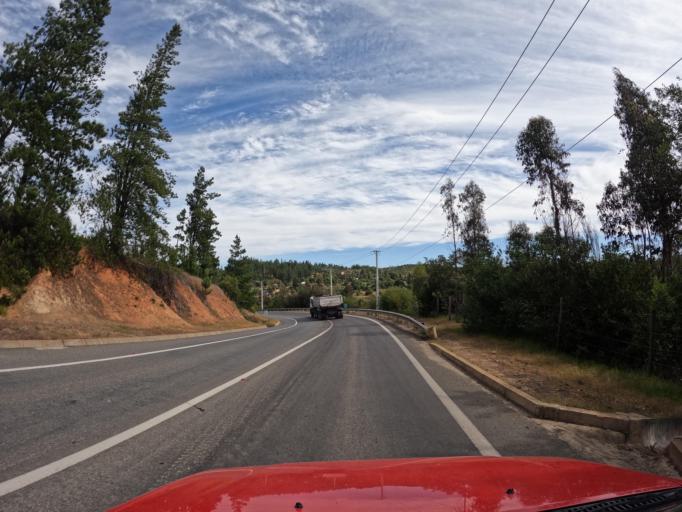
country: CL
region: Maule
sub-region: Provincia de Talca
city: Talca
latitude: -35.1682
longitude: -71.9739
